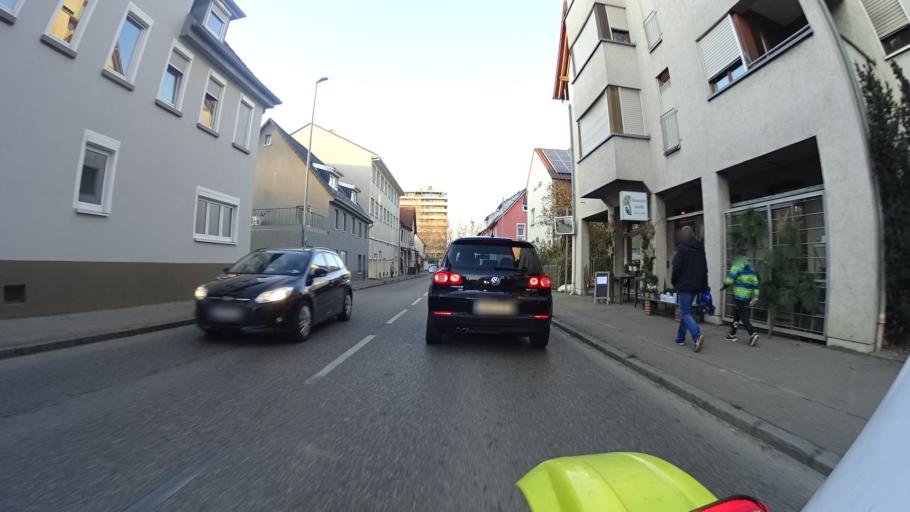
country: DE
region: Baden-Wuerttemberg
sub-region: Regierungsbezirk Stuttgart
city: Eislingen
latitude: 48.6845
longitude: 9.6873
